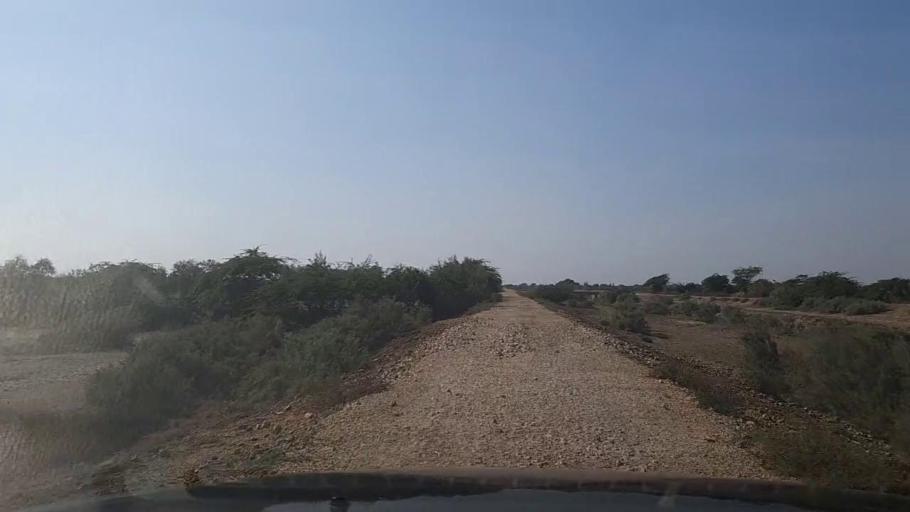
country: PK
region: Sindh
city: Gharo
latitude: 24.7113
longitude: 67.7473
